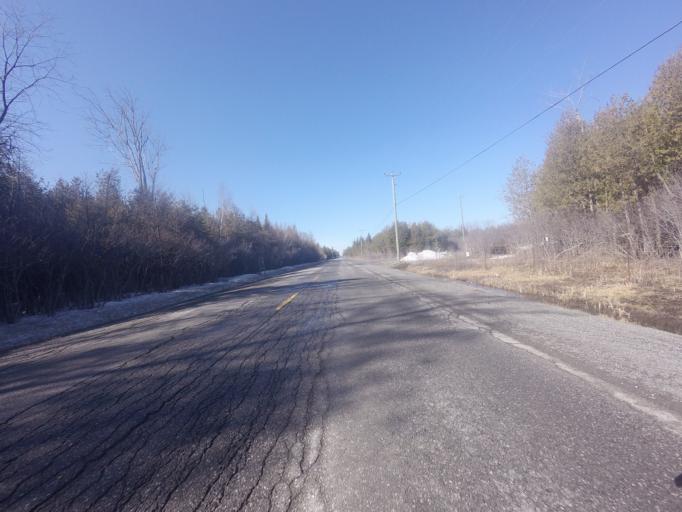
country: CA
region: Ontario
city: Bells Corners
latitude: 45.2097
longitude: -75.9735
